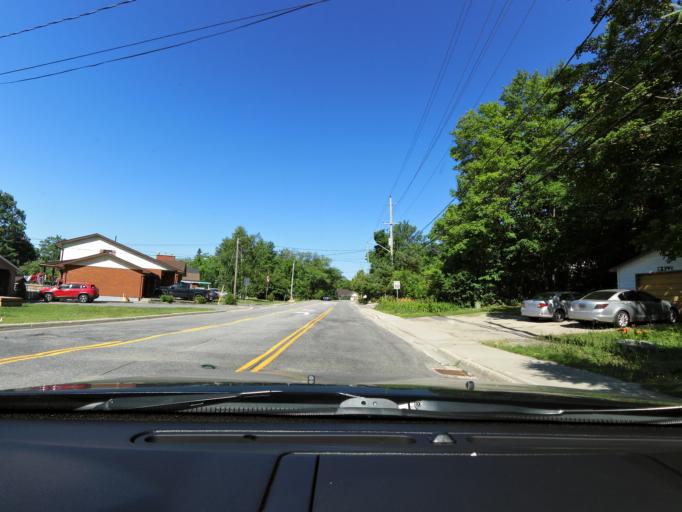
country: CA
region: Ontario
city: Huntsville
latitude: 45.3313
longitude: -79.2156
